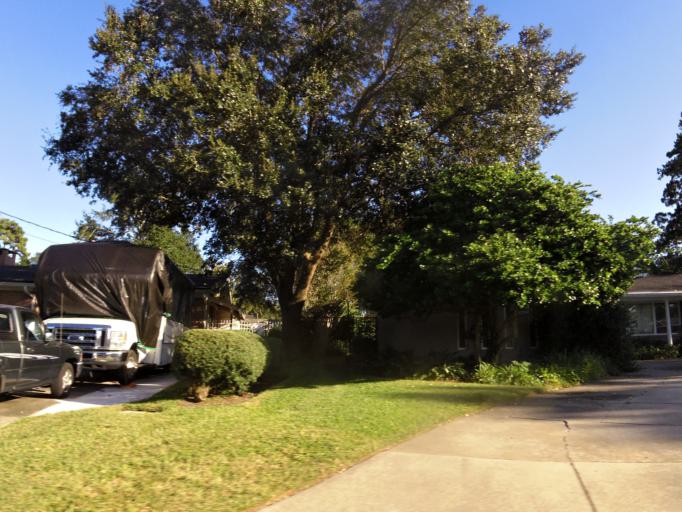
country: US
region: Florida
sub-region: Duval County
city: Jacksonville
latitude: 30.2526
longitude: -81.6333
